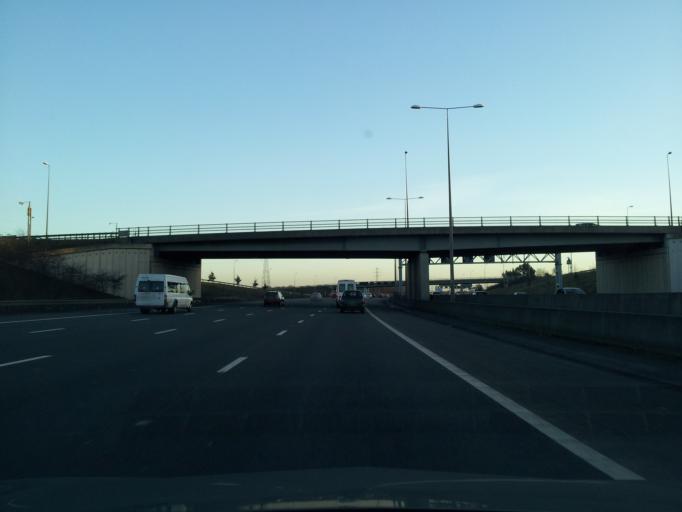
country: GB
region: England
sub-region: Luton
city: Luton
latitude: 51.8537
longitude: -0.4233
